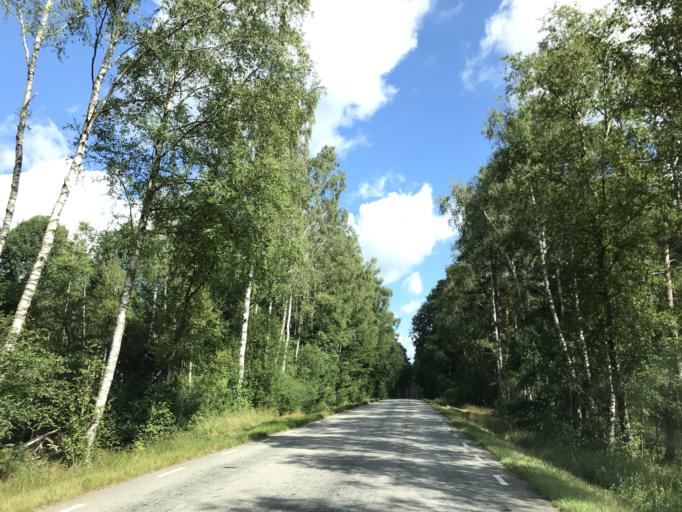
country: SE
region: Halland
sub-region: Laholms Kommun
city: Knared
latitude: 56.4521
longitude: 13.3203
